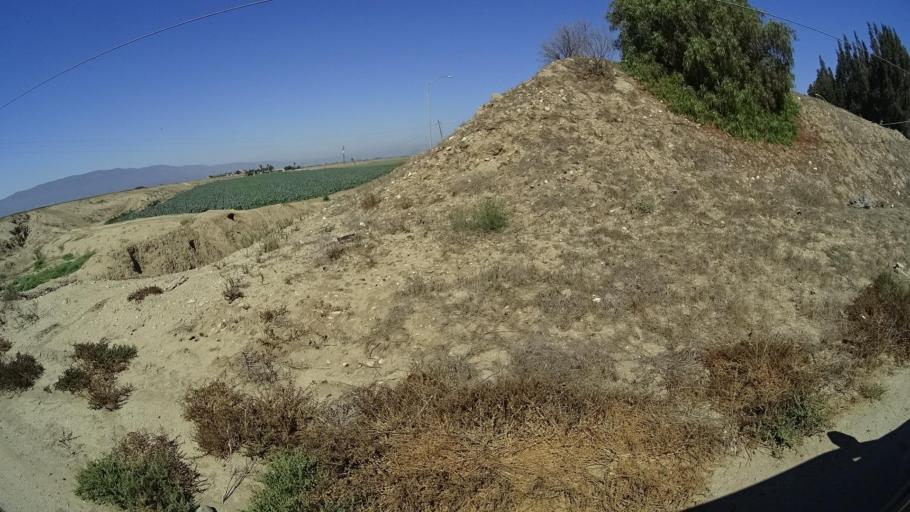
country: US
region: California
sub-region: Monterey County
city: Greenfield
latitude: 36.3401
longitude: -121.2244
